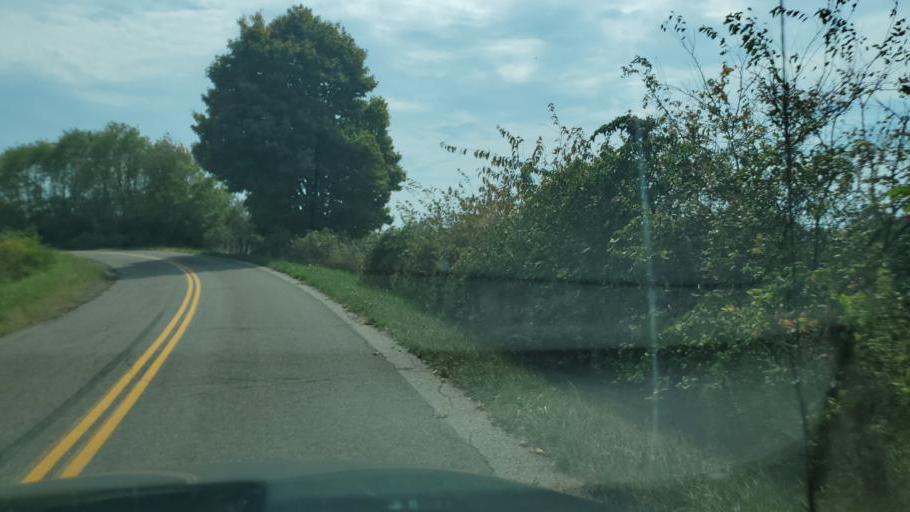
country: US
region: Ohio
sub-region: Muskingum County
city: Zanesville
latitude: 39.9402
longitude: -82.0816
